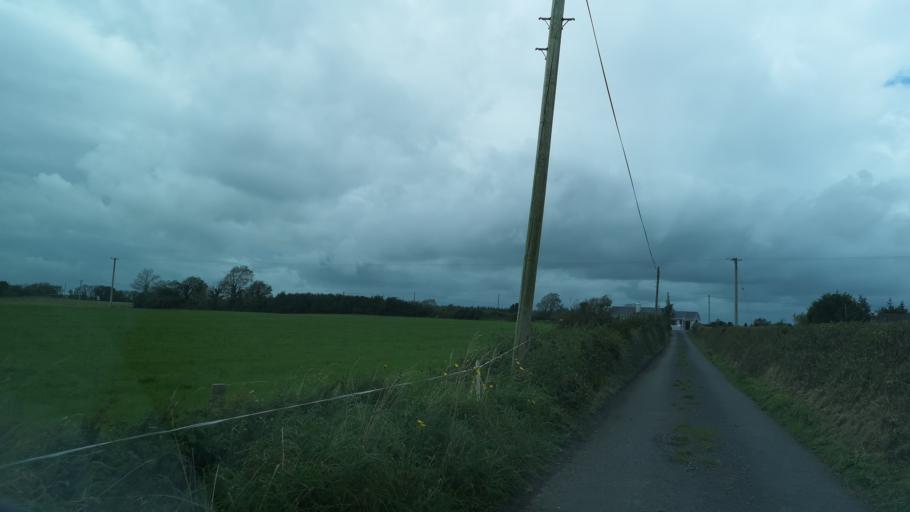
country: IE
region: Connaught
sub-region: County Galway
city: Athenry
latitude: 53.2978
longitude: -8.6825
